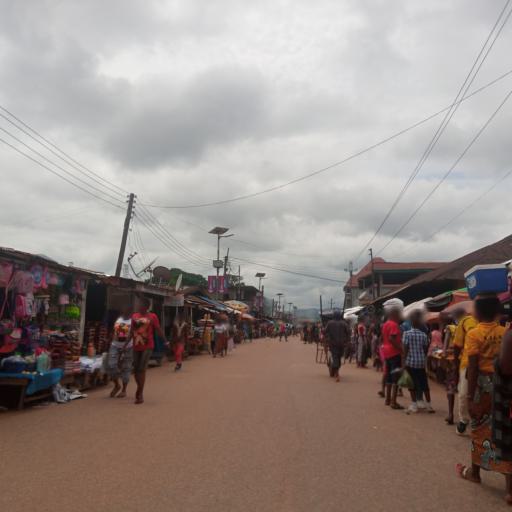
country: SL
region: Eastern Province
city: Kenema
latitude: 7.8768
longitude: -11.1917
